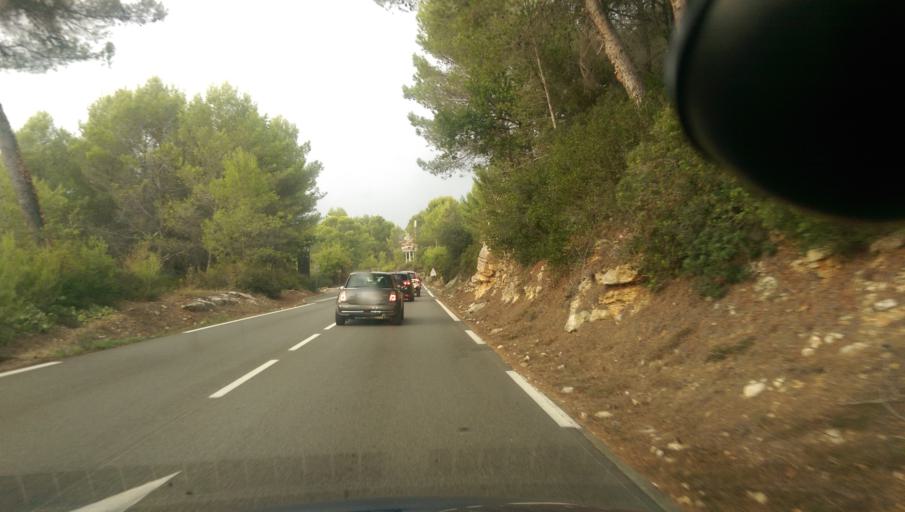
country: FR
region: Provence-Alpes-Cote d'Azur
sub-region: Departement des Alpes-Maritimes
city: Valbonne
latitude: 43.6279
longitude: 7.0424
